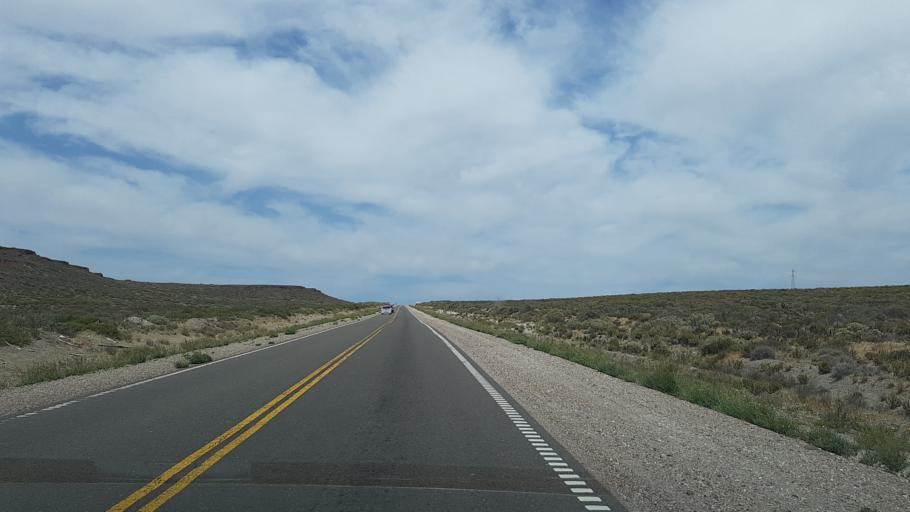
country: AR
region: Neuquen
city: Piedra del Aguila
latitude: -39.9756
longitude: -70.0323
